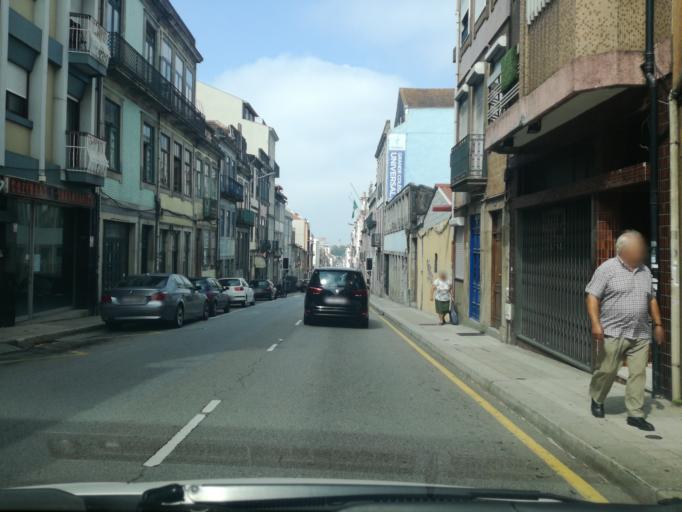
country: PT
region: Porto
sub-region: Porto
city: Porto
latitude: 41.1556
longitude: -8.6146
